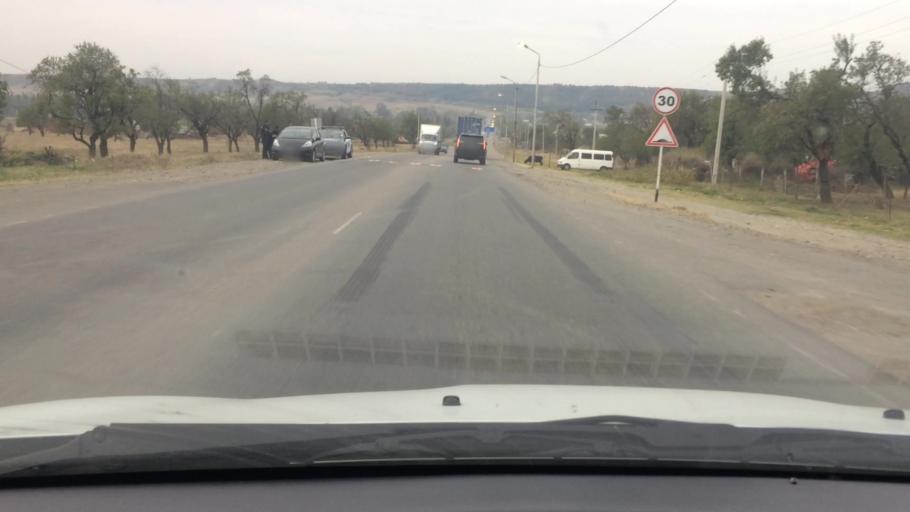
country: GE
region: T'bilisi
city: Tbilisi
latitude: 41.6180
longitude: 44.7935
